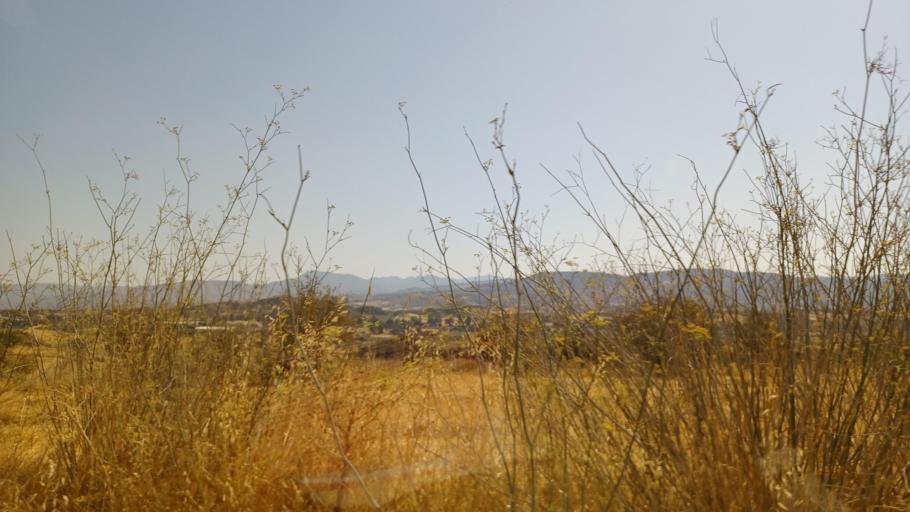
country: CY
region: Pafos
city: Polis
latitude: 35.0158
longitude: 32.4189
